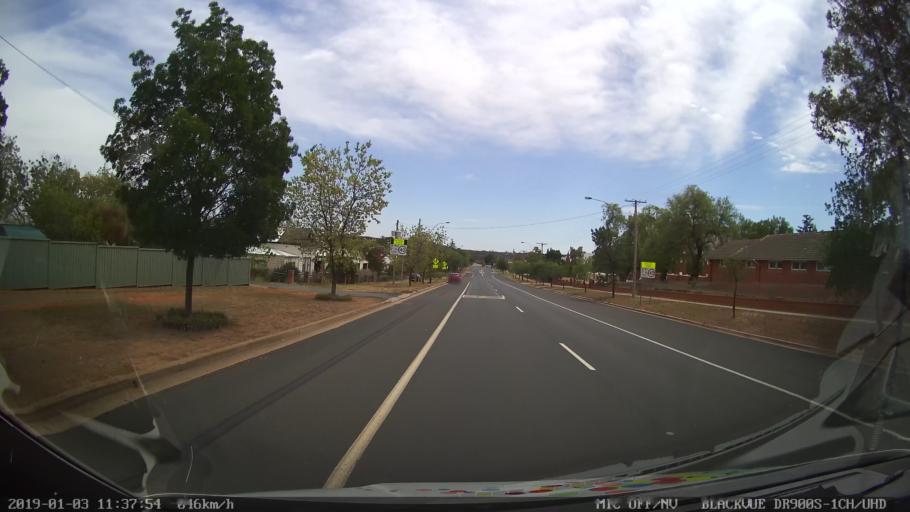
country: AU
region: New South Wales
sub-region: Weddin
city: Grenfell
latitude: -33.8999
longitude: 148.1618
